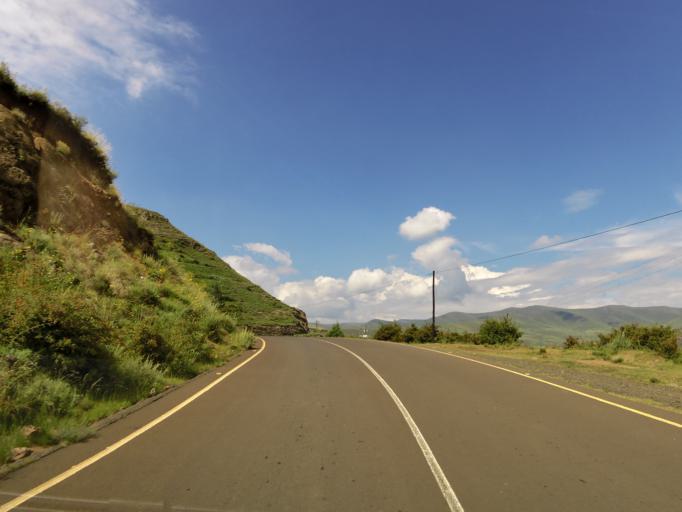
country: LS
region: Thaba-Tseka
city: Thaba-Tseka
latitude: -29.1403
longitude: 28.4903
